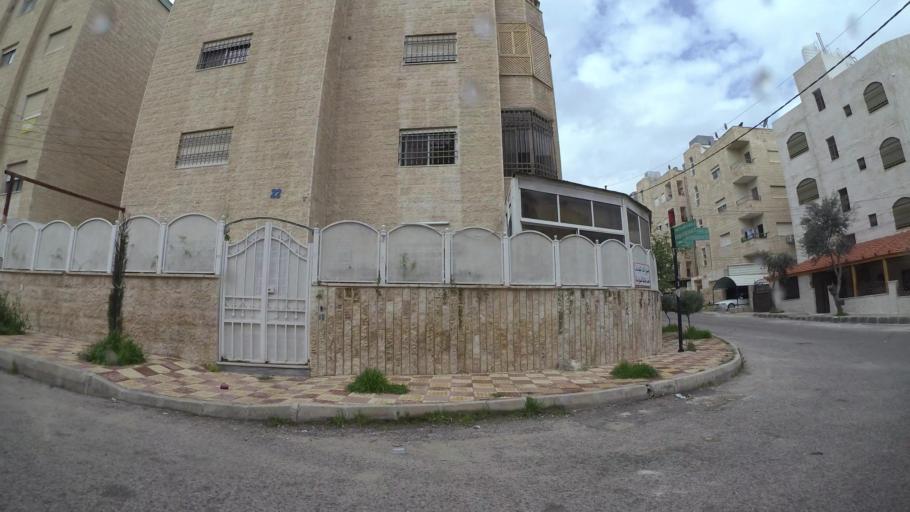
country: JO
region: Amman
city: Amman
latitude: 31.9859
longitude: 35.9293
